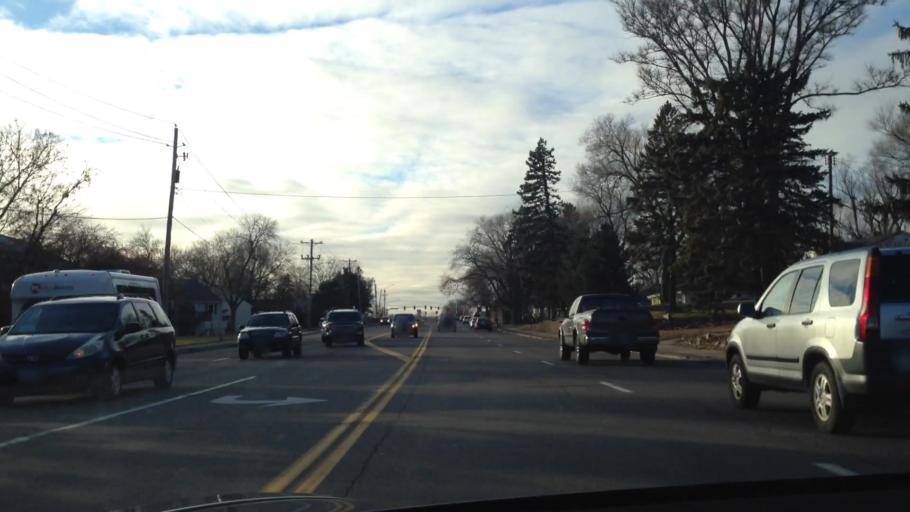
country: US
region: Minnesota
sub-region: Hennepin County
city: New Hope
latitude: 45.0334
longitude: -93.3911
